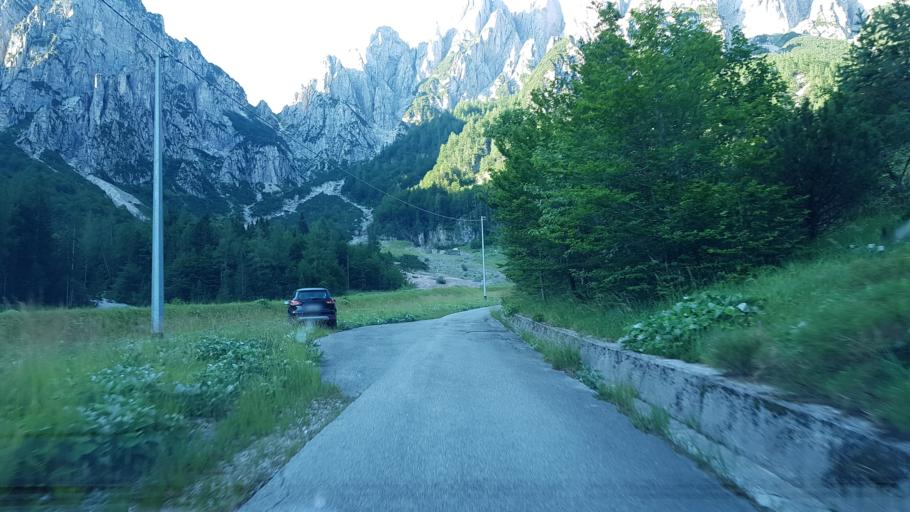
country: IT
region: Friuli Venezia Giulia
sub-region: Provincia di Udine
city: Pontebba
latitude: 46.4853
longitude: 13.2535
